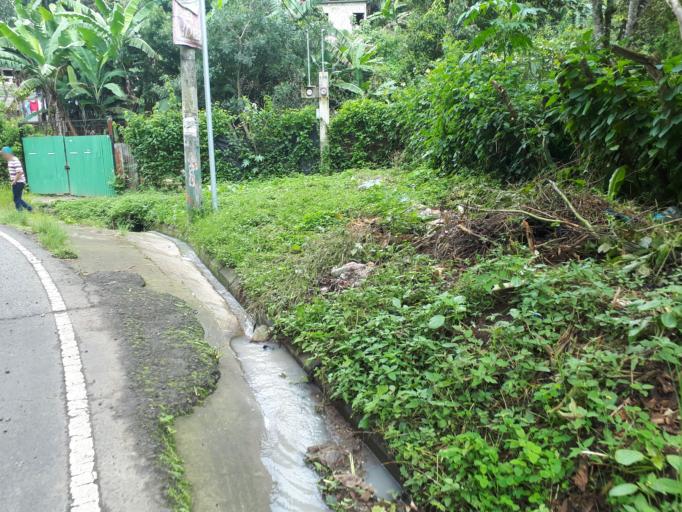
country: GT
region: Guatemala
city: Villa Canales
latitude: 14.4557
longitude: -90.5074
